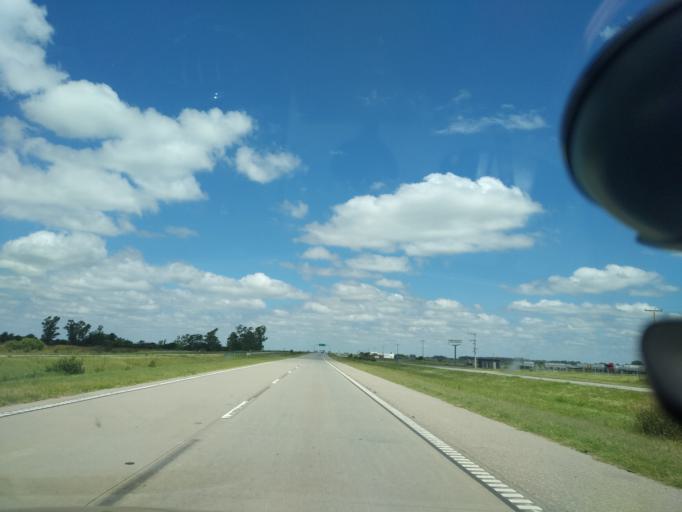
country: AR
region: Cordoba
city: Villa Maria
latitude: -32.3762
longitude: -63.2155
